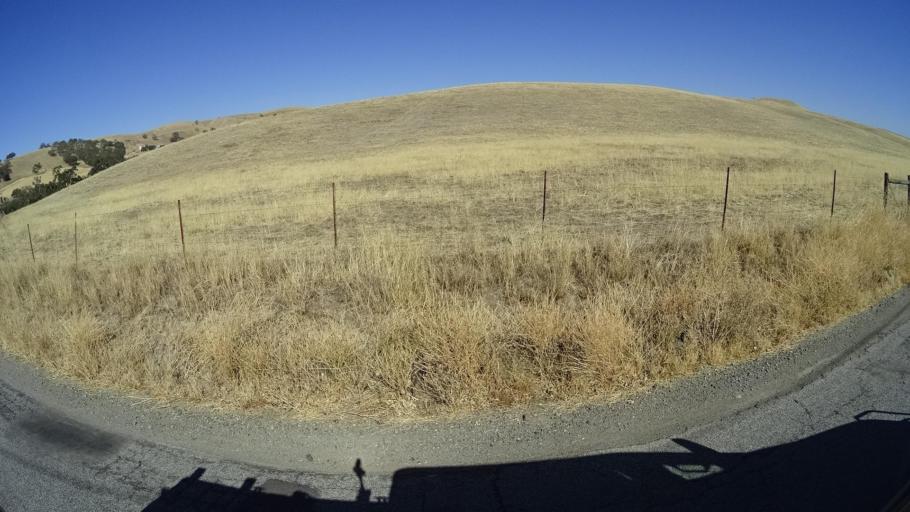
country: US
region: California
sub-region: San Luis Obispo County
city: San Miguel
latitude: 35.7907
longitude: -120.5804
